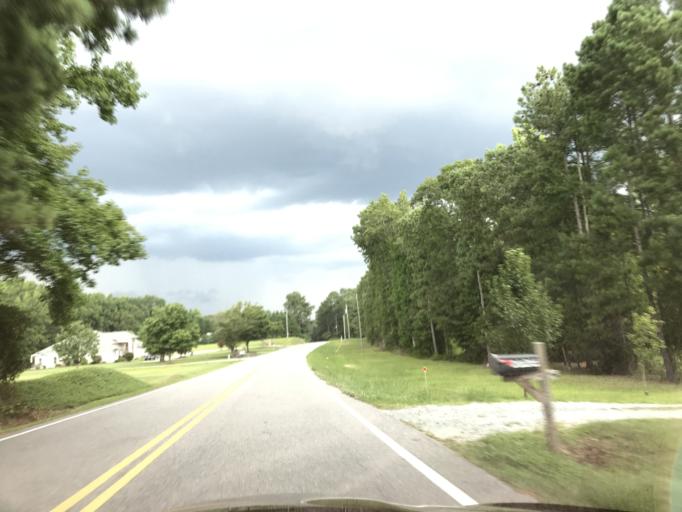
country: US
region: North Carolina
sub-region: Johnston County
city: Four Oaks
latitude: 35.5118
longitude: -78.4731
